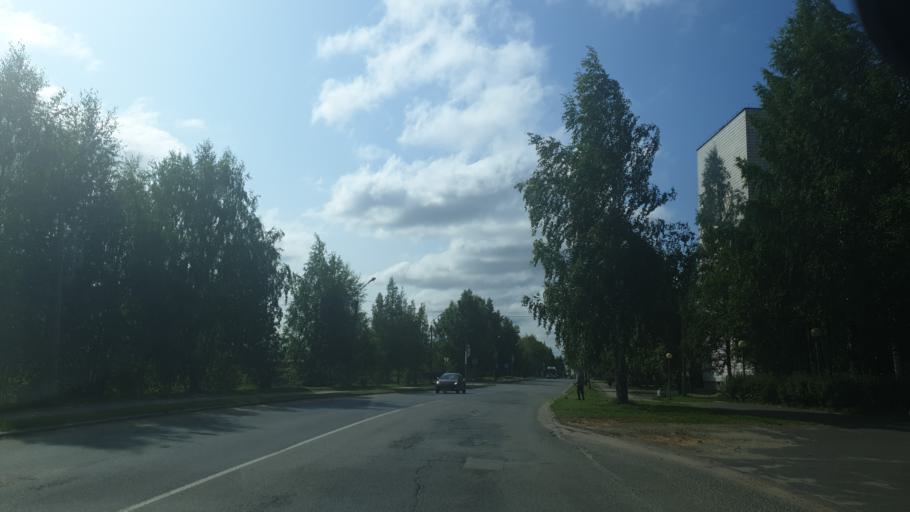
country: RU
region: Komi Republic
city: Ezhva
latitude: 61.7949
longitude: 50.7510
